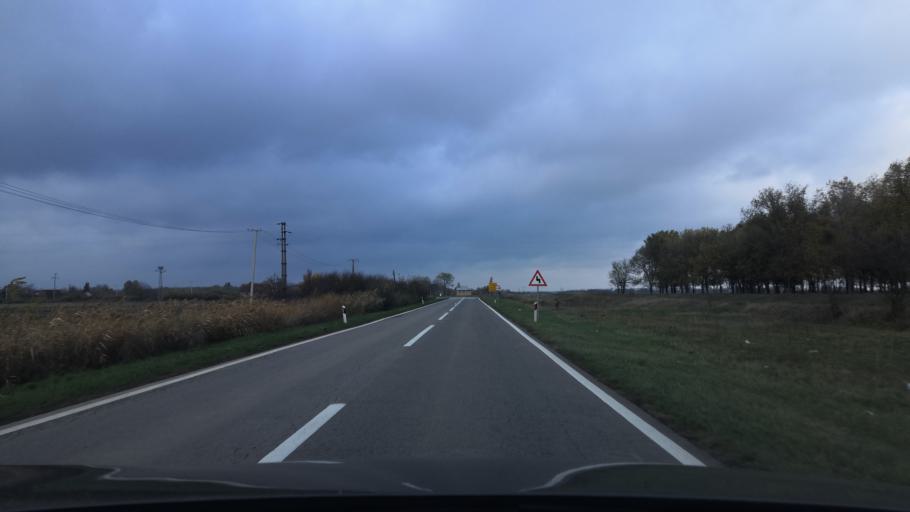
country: RS
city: Sanad
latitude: 45.9736
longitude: 20.1203
